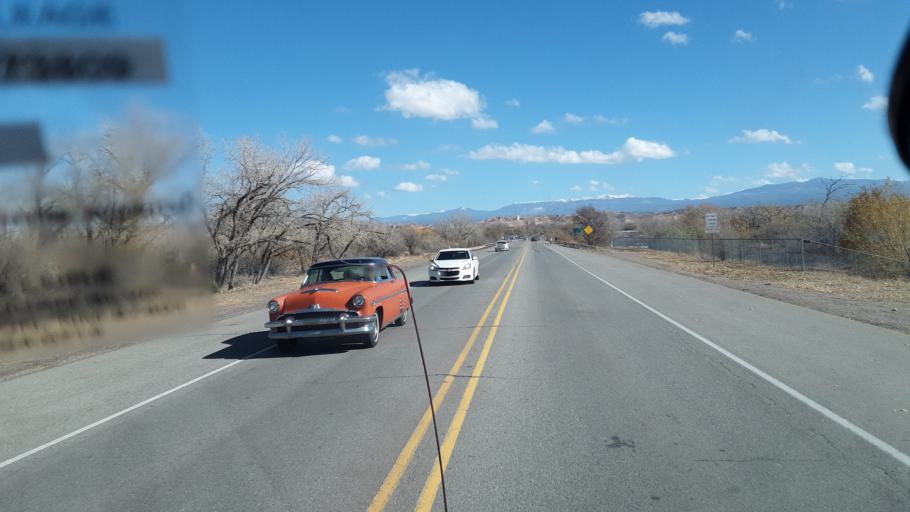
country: US
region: New Mexico
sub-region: Rio Arriba County
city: Espanola
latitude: 36.0082
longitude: -106.0748
